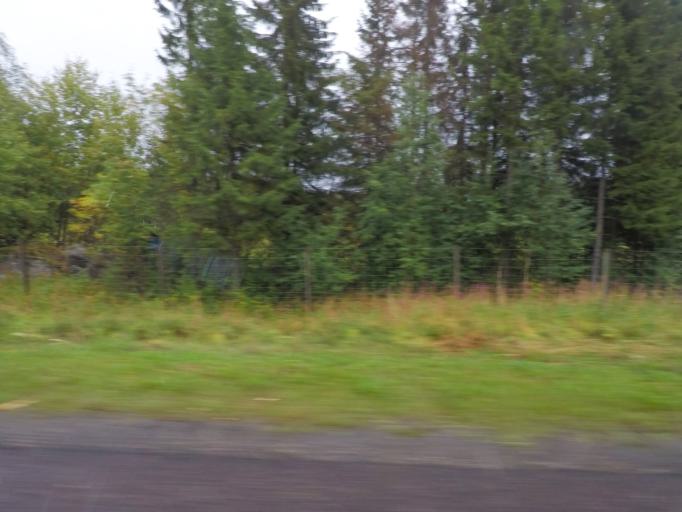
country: FI
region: Northern Savo
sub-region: Varkaus
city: Varkaus
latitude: 62.2431
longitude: 27.8867
